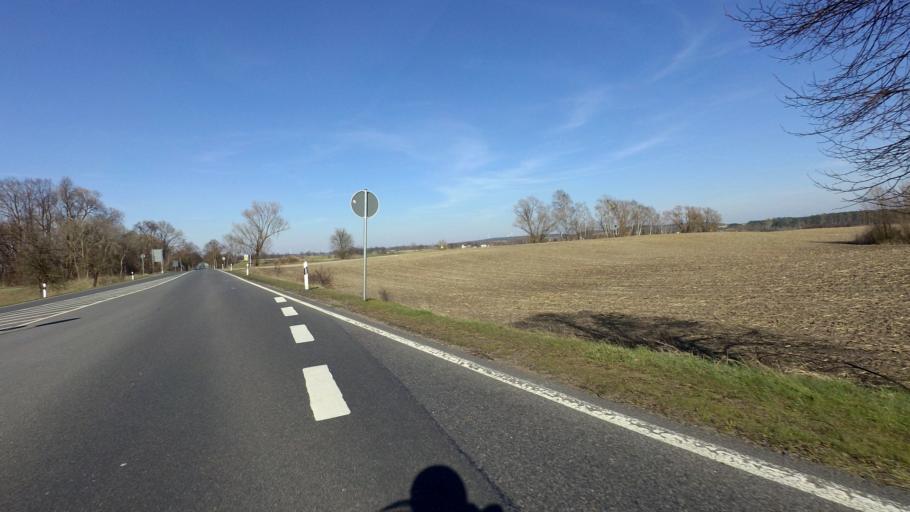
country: DE
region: Brandenburg
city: Angermunde
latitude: 52.9711
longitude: 13.9661
